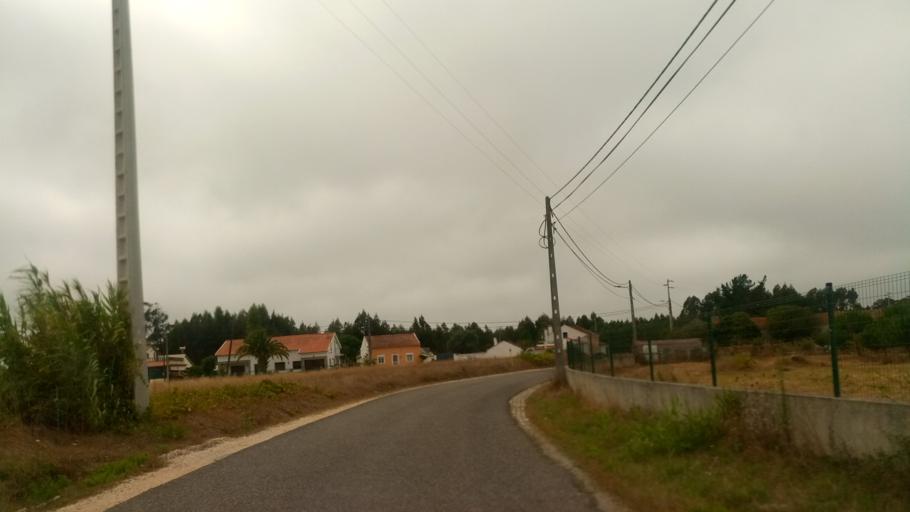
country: PT
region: Leiria
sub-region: Caldas da Rainha
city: Caldas da Rainha
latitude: 39.4222
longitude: -9.1503
